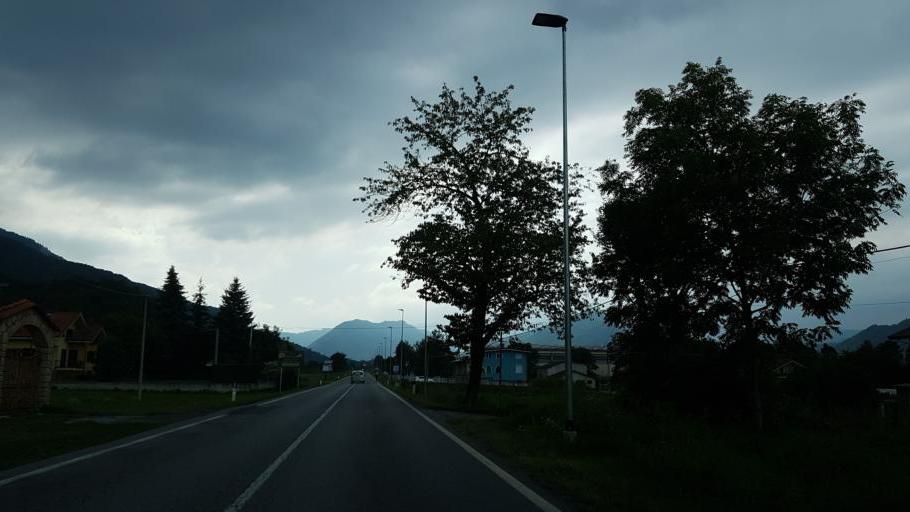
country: IT
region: Piedmont
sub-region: Provincia di Cuneo
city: Roccasparvera
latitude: 44.3342
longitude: 7.4530
